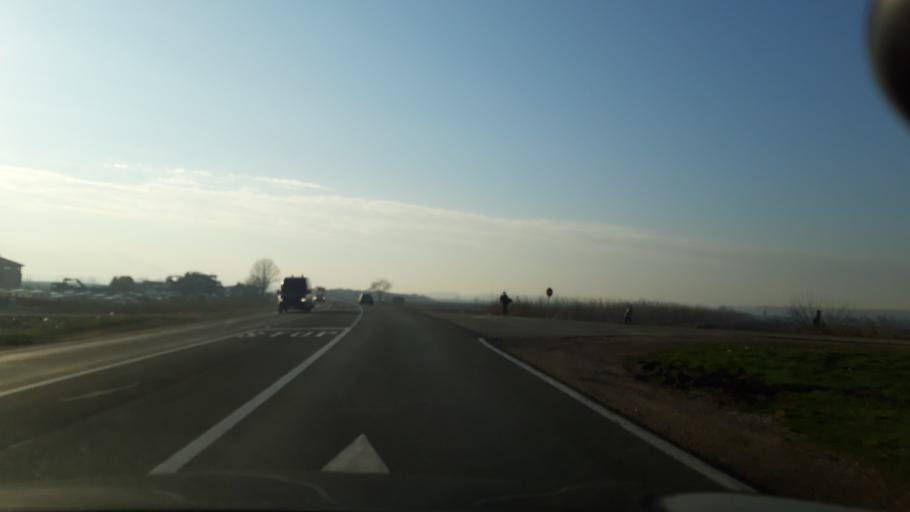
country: RS
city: Klenak
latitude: 44.7857
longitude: 19.7231
